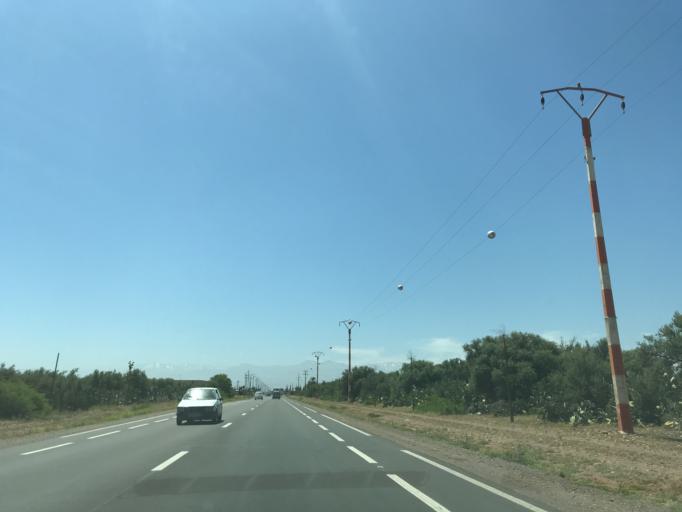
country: MA
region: Marrakech-Tensift-Al Haouz
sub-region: Marrakech
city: Marrakesh
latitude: 31.5392
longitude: -7.9996
